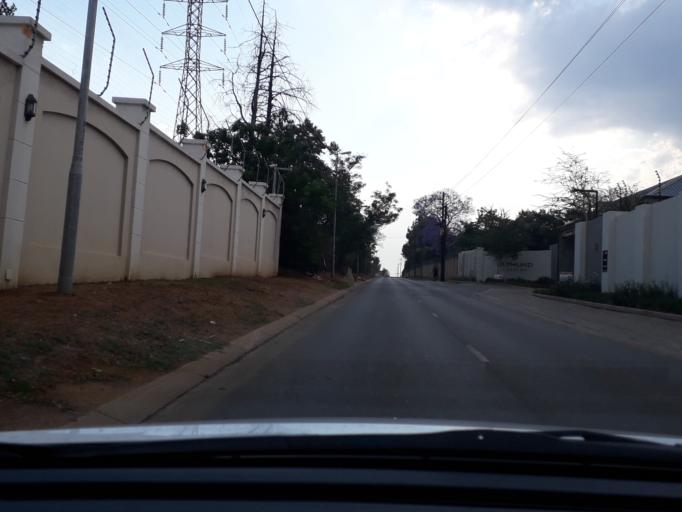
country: ZA
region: Gauteng
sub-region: City of Johannesburg Metropolitan Municipality
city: Diepsloot
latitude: -26.0001
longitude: 27.9910
